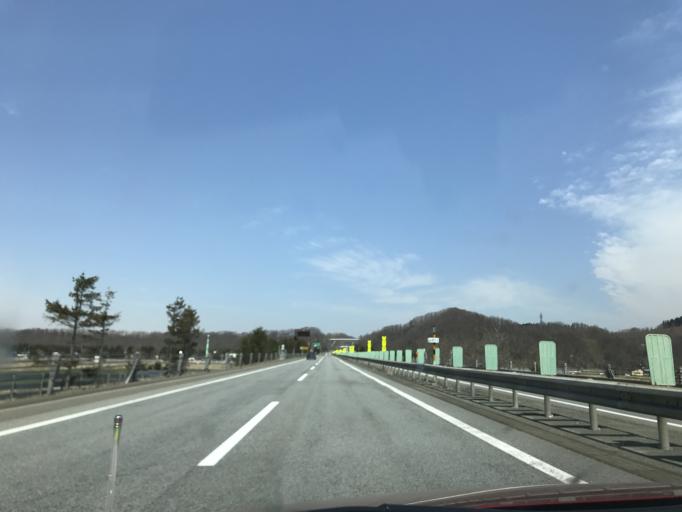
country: JP
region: Hokkaido
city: Iwamizawa
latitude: 43.2374
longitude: 141.8304
